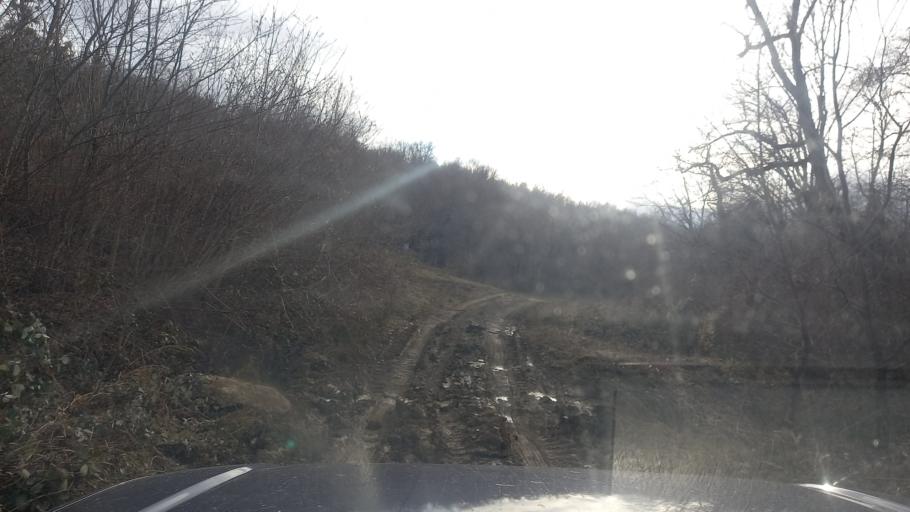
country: RU
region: Krasnodarskiy
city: Neftegorsk
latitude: 44.2030
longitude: 39.7043
